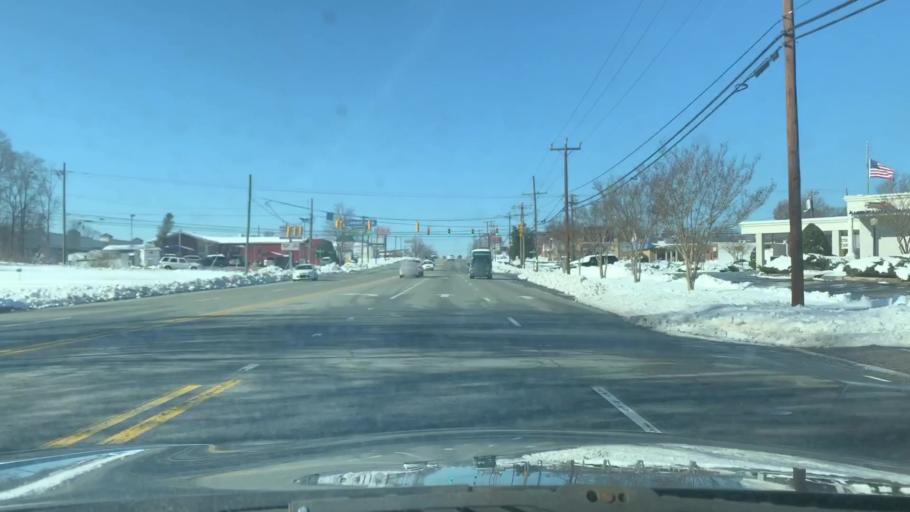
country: US
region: North Carolina
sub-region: Alamance County
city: Graham
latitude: 36.0936
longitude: -79.3979
